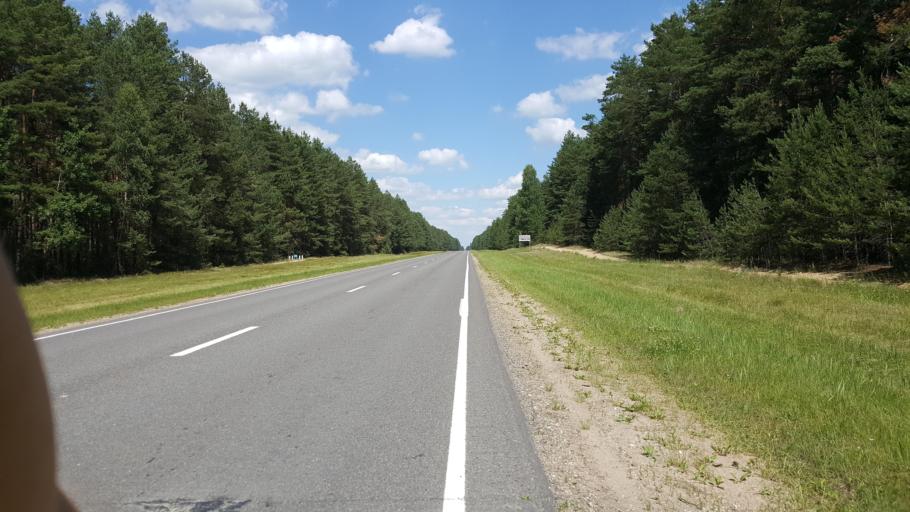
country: BY
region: Brest
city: Kamyanyuki
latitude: 52.5214
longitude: 23.7901
